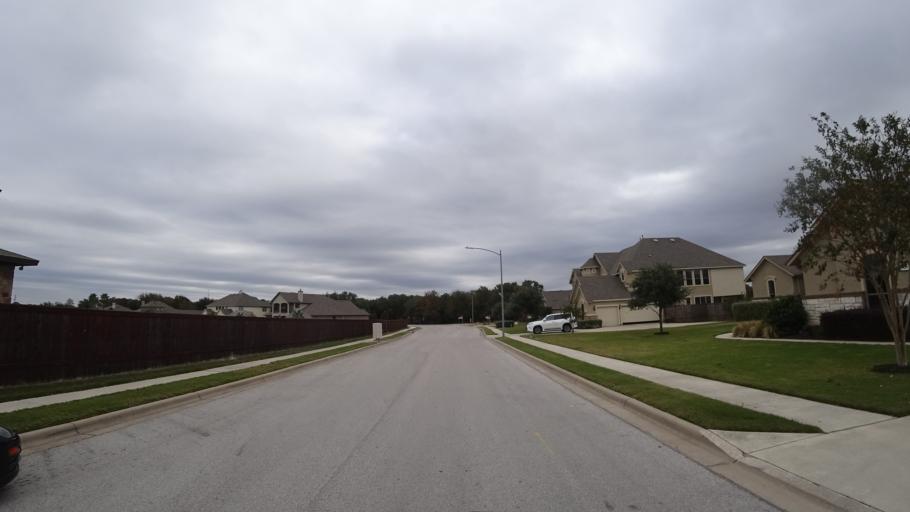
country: US
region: Texas
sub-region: Travis County
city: Shady Hollow
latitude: 30.1463
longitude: -97.8578
